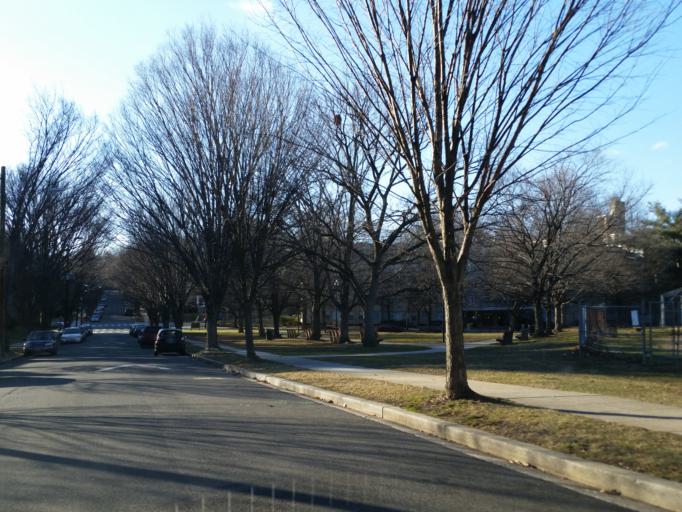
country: US
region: Maryland
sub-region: Montgomery County
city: Silver Spring
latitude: 38.9700
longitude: -77.0317
